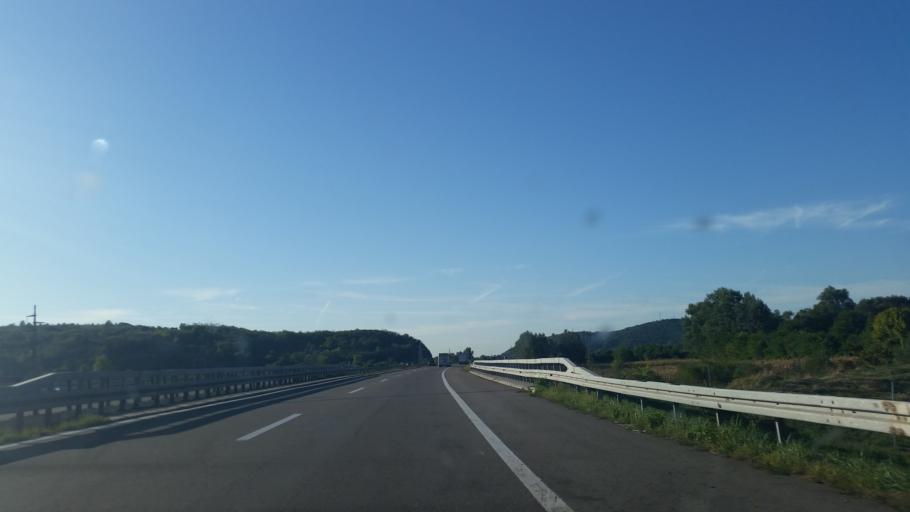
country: RS
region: Central Serbia
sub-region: Pomoravski Okrug
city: Jagodina
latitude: 44.0442
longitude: 21.2434
